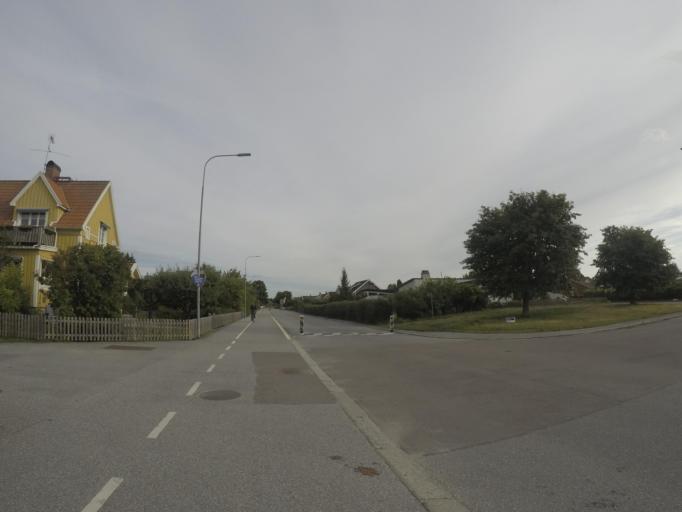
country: SE
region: OErebro
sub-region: Orebro Kommun
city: Orebro
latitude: 59.2592
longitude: 15.2485
